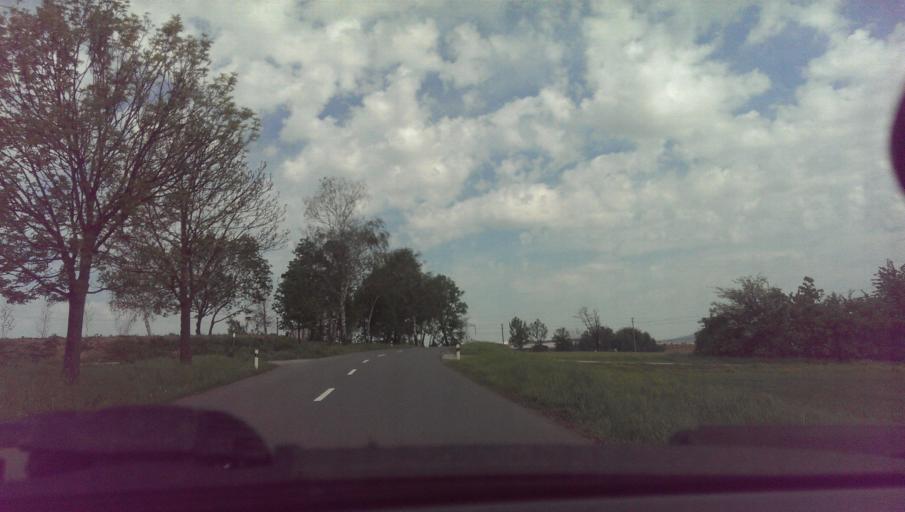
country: CZ
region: Zlin
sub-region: Okres Zlin
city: Otrokovice
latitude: 49.2431
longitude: 17.5389
